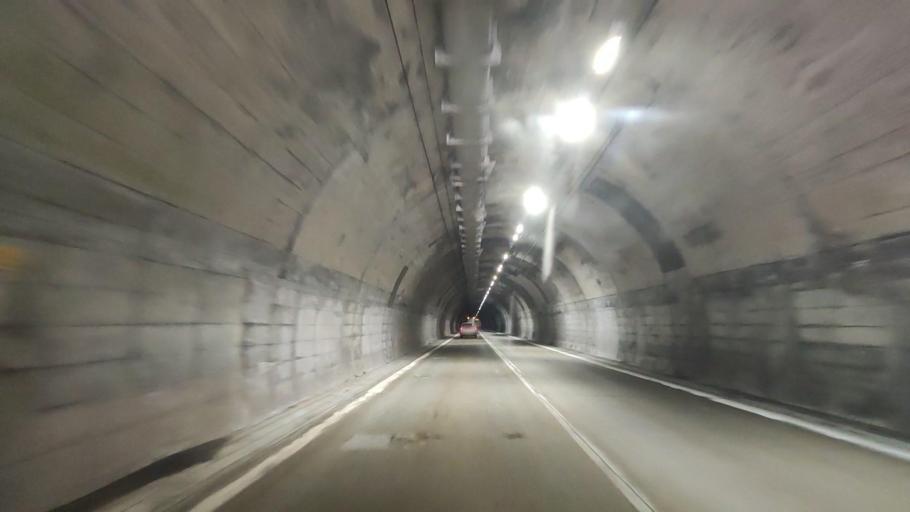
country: JP
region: Toyama
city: Yatsuomachi-higashikumisaka
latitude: 36.4393
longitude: 137.2743
